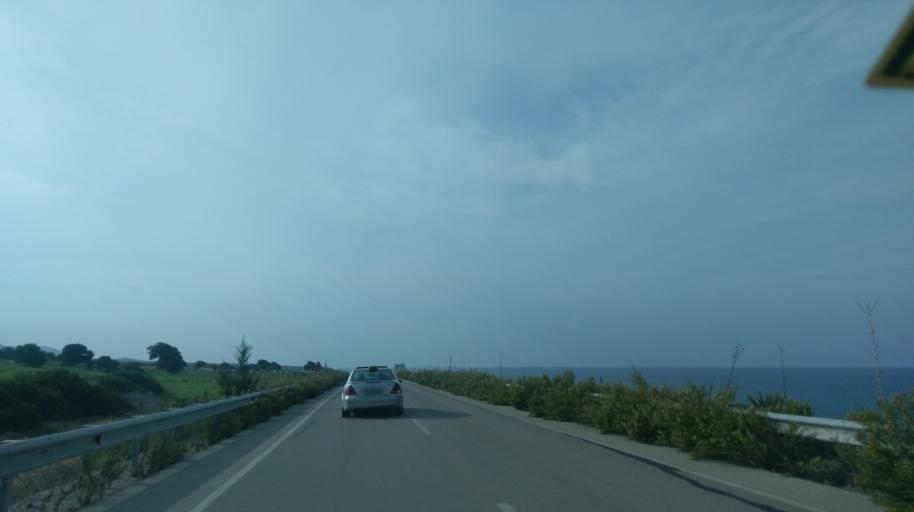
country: CY
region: Ammochostos
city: Trikomo
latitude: 35.4113
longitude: 33.8488
